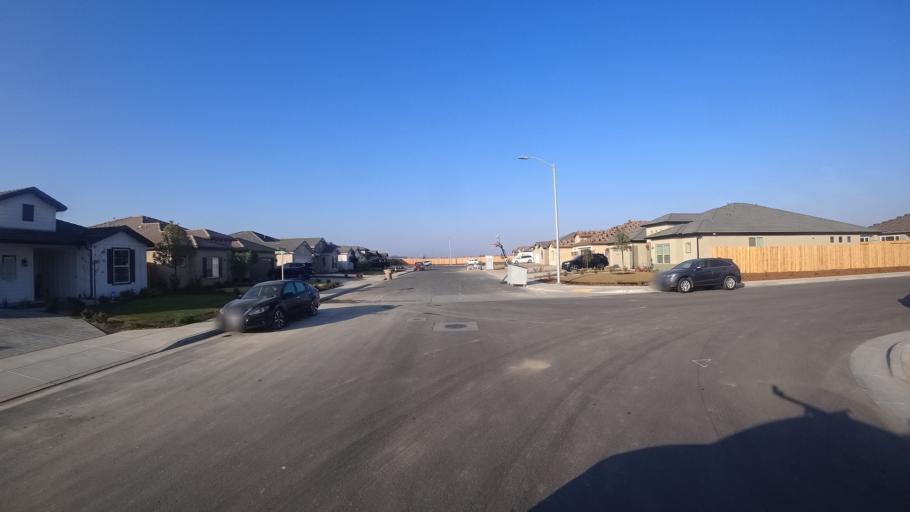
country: US
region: California
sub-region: Kern County
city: Greenacres
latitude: 35.2938
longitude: -119.1130
